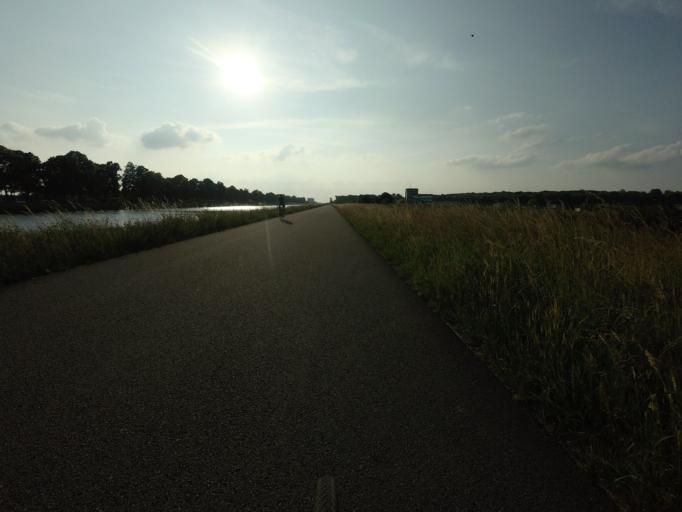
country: BE
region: Flanders
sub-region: Provincie Antwerpen
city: Schilde
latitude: 51.2172
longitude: 4.5699
